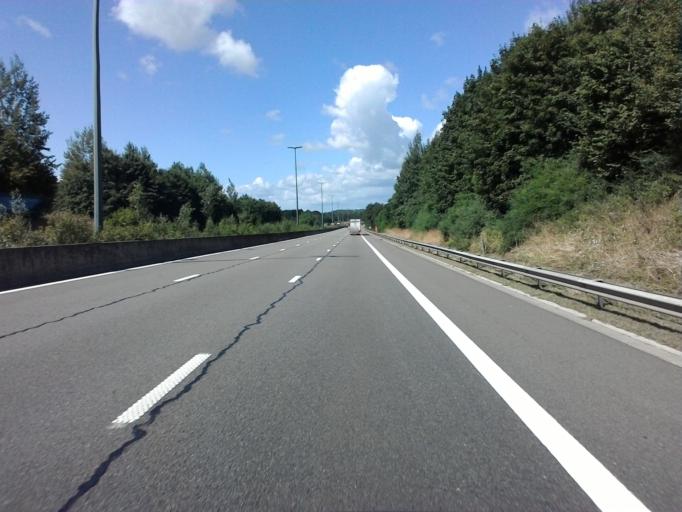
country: BE
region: Wallonia
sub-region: Province du Luxembourg
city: Habay-la-Vieille
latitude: 49.6959
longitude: 5.6819
